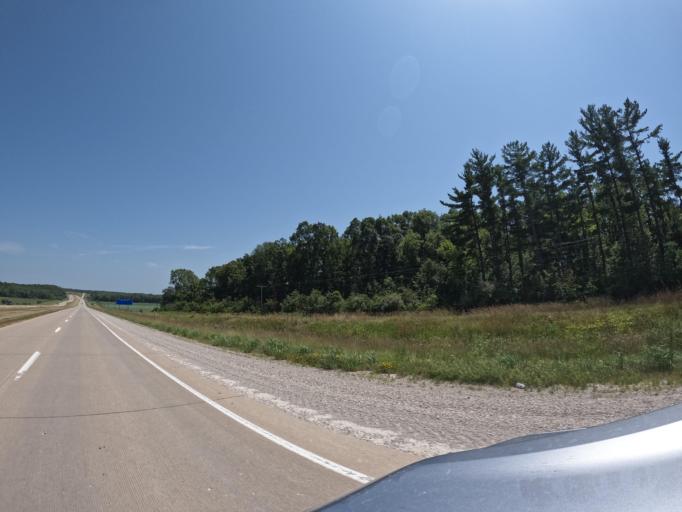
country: US
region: Iowa
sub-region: Henry County
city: Mount Pleasant
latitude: 40.9734
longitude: -91.6554
